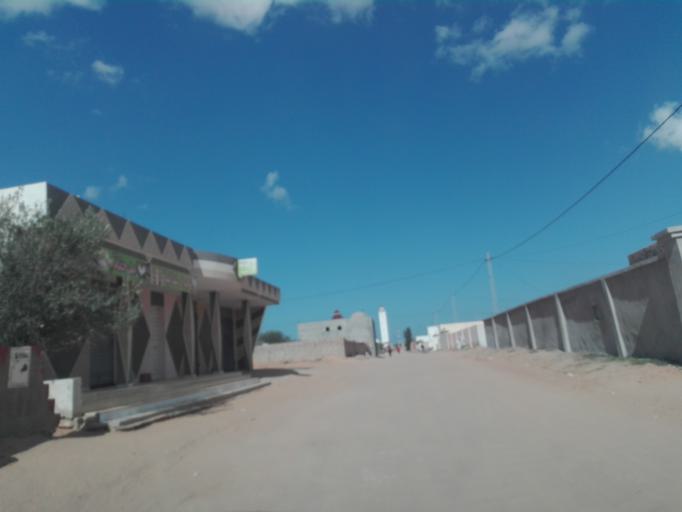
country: TN
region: Madanin
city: Bin Qirdan
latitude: 33.1575
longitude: 11.1943
